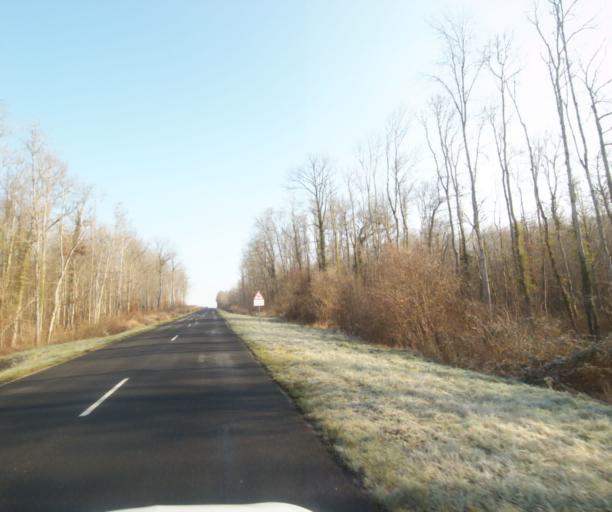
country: FR
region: Champagne-Ardenne
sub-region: Departement de la Haute-Marne
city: Laneuville-a-Remy
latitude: 48.4900
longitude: 4.8375
